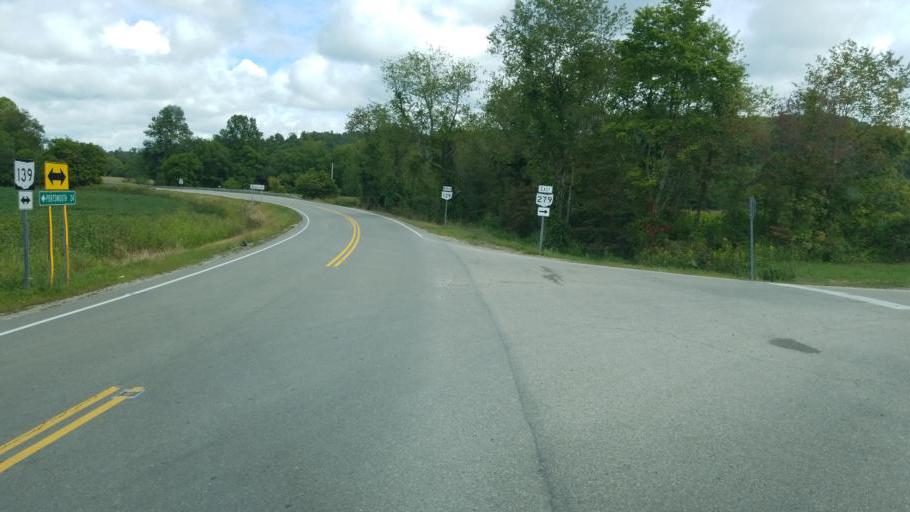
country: US
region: Ohio
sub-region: Jackson County
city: Oak Hill
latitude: 38.8837
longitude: -82.7445
